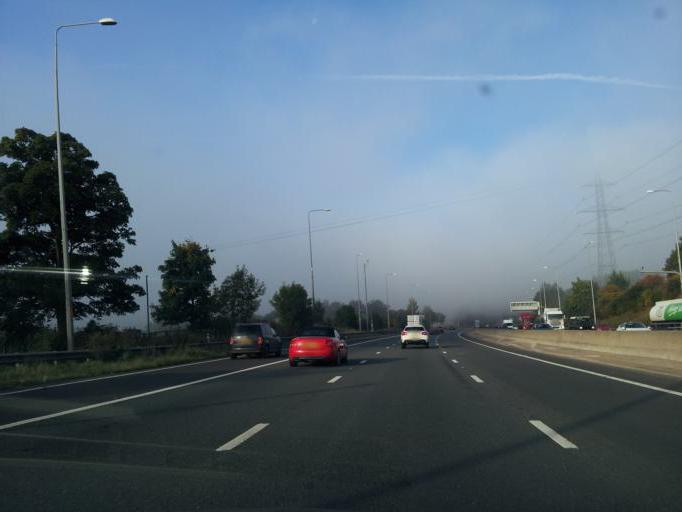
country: GB
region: England
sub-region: City and Borough of Leeds
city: Drighlington
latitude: 53.7410
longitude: -1.6836
